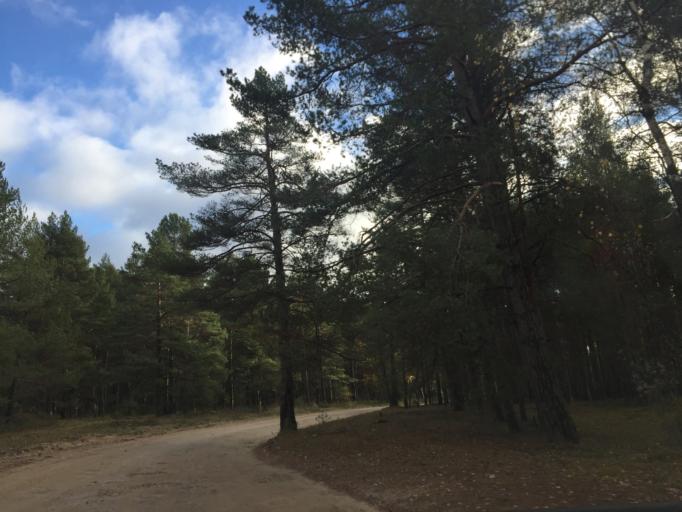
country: LV
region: Carnikava
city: Carnikava
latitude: 57.1428
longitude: 24.2648
